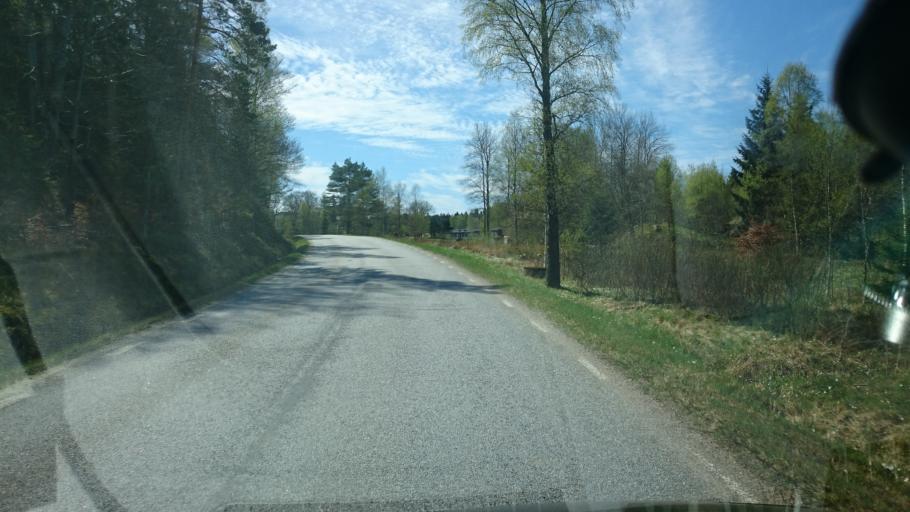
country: SE
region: Vaestra Goetaland
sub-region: Munkedals Kommun
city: Munkedal
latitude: 58.4190
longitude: 11.6862
